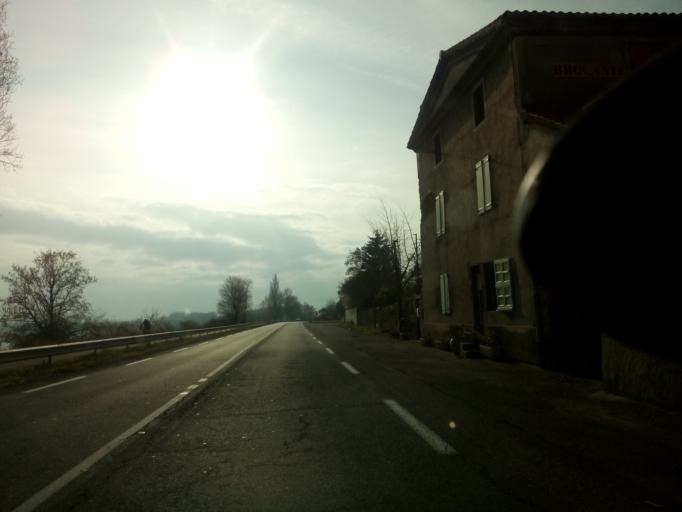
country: FR
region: Rhone-Alpes
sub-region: Departement de l'Isere
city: Les Roches-de-Condrieu
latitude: 45.4526
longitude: 4.7539
